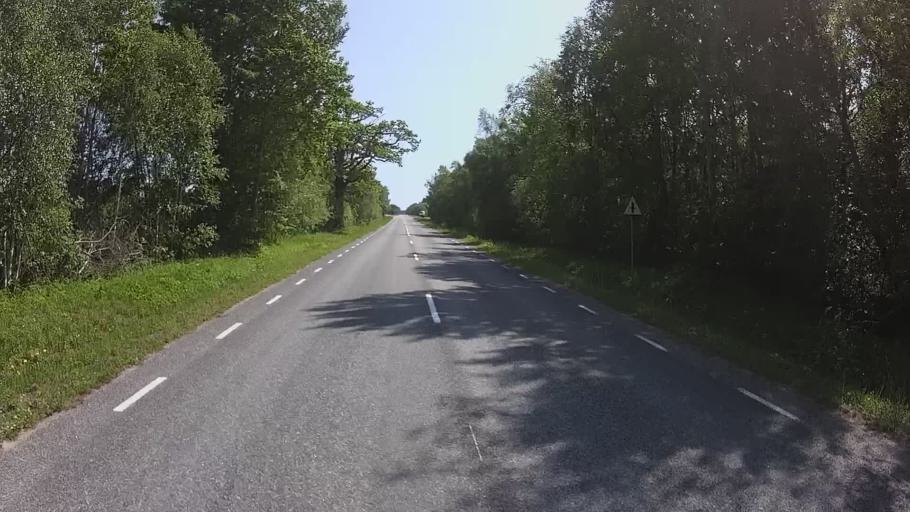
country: EE
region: Saare
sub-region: Kuressaare linn
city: Kuressaare
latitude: 58.3659
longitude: 22.0534
